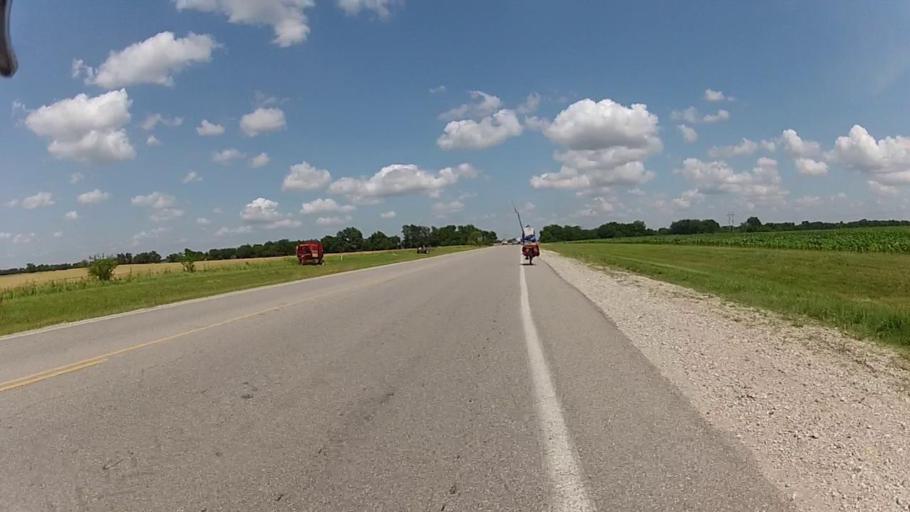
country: US
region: Kansas
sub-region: Labette County
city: Altamont
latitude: 37.1935
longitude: -95.2658
